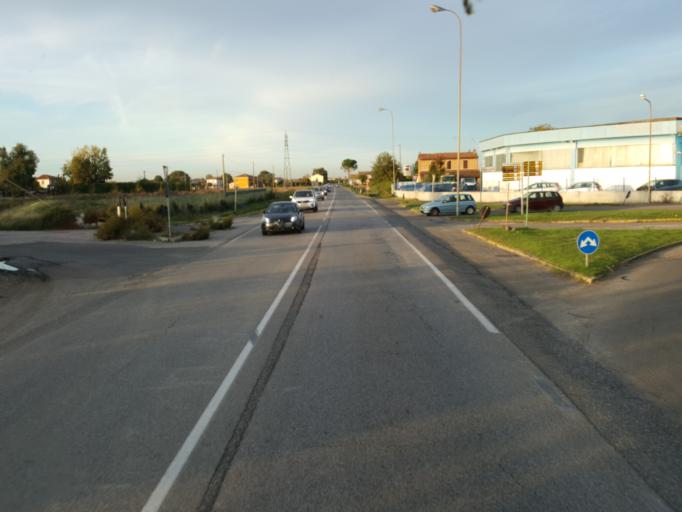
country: IT
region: Emilia-Romagna
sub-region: Provincia di Ravenna
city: Faenza
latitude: 44.3029
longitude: 11.8852
